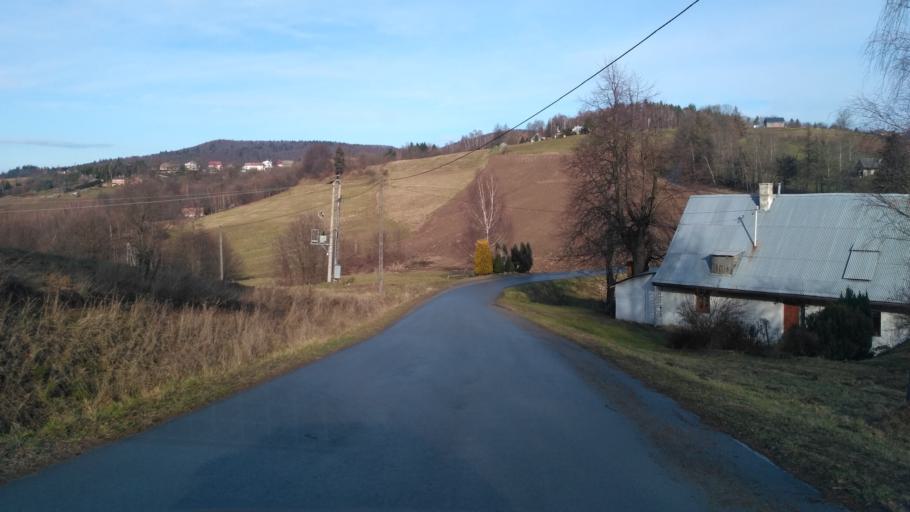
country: PL
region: Subcarpathian Voivodeship
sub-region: Powiat krosnienski
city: Korczyna
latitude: 49.7330
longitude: 21.7851
